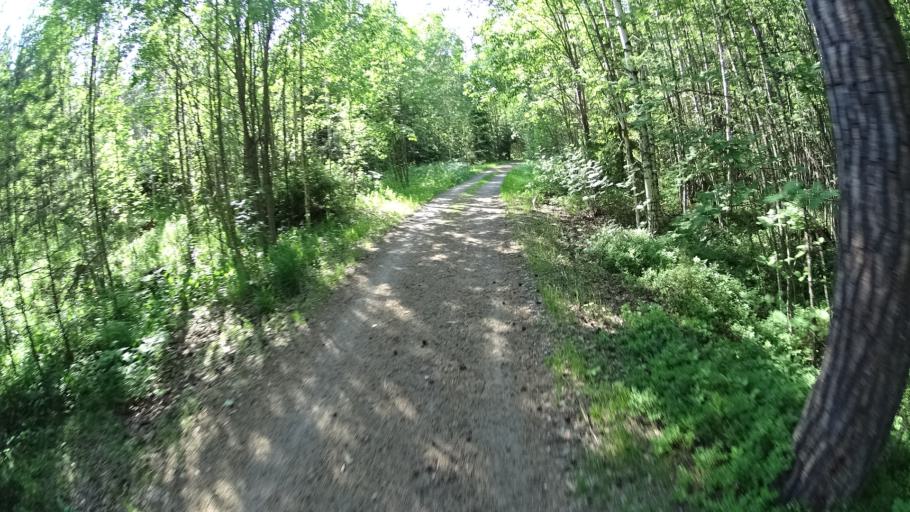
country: FI
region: Uusimaa
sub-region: Helsinki
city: Vantaa
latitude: 60.2358
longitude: 25.1768
